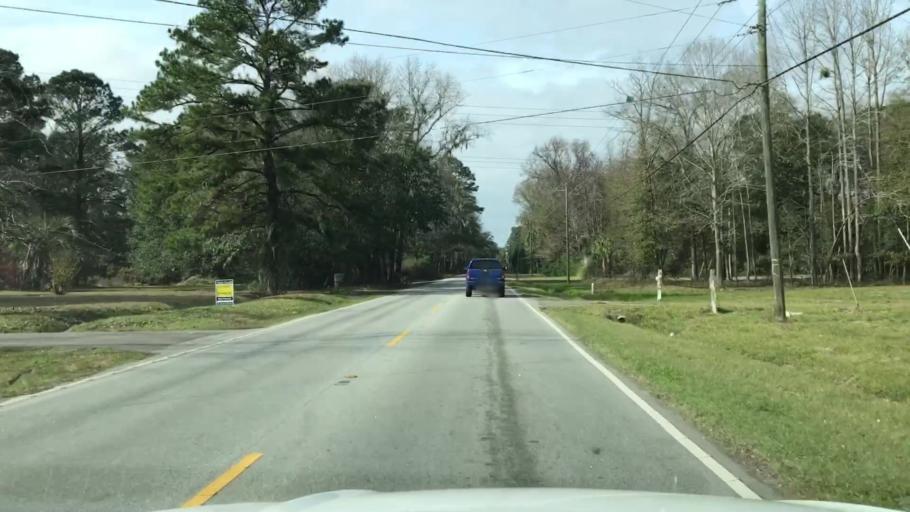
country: US
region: South Carolina
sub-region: Charleston County
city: Shell Point
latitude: 32.7787
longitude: -80.1001
